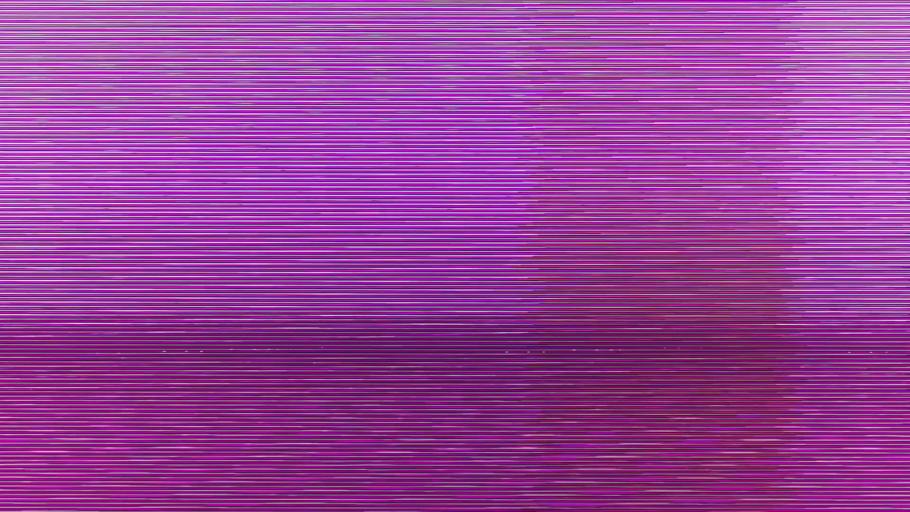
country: US
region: Wisconsin
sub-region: Racine County
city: Waterford
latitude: 42.7620
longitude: -88.1995
